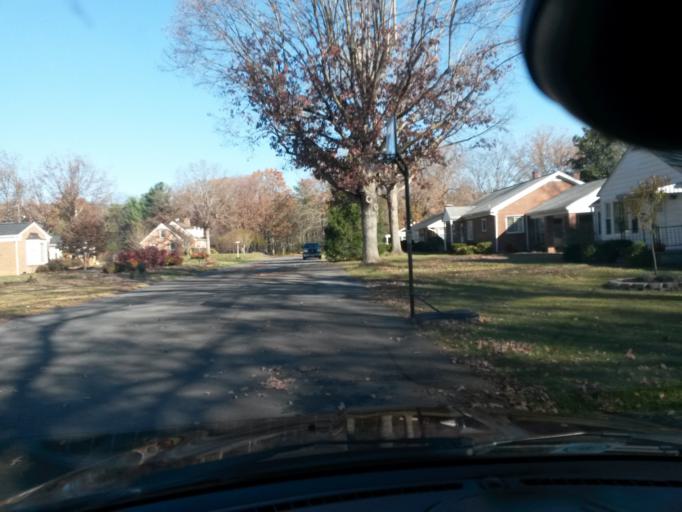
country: US
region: Virginia
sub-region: Alleghany County
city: Clifton Forge
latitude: 37.8273
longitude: -79.8242
